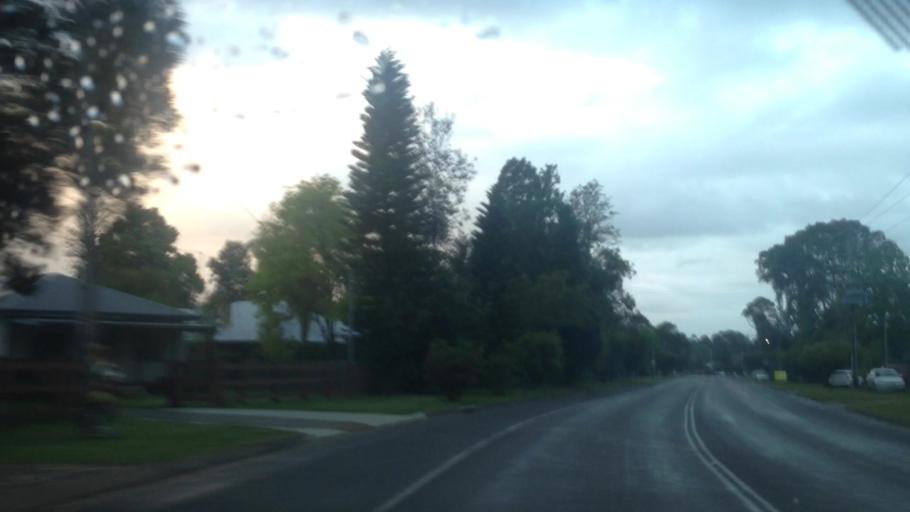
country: AU
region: New South Wales
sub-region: Lake Macquarie Shire
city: Cooranbong
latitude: -33.0821
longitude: 151.4472
